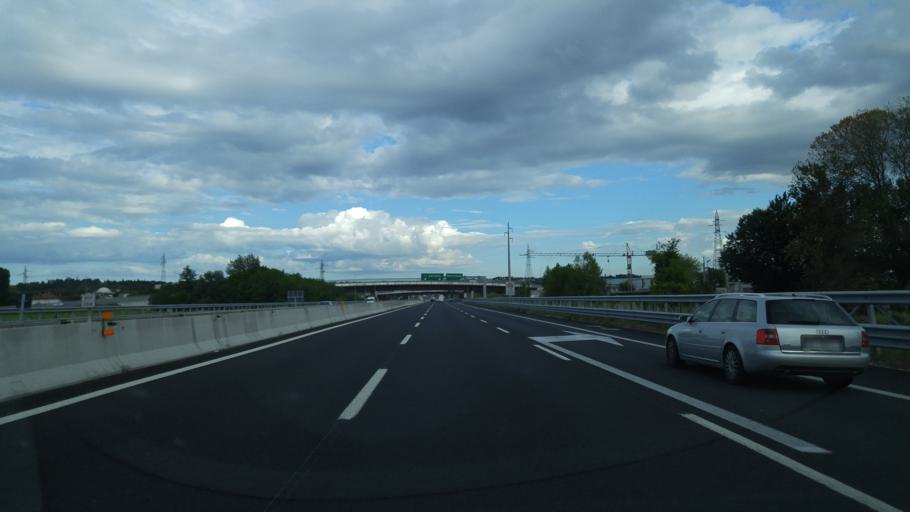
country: IT
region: Emilia-Romagna
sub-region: Provincia di Rimini
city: Riccione
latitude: 43.9889
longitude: 12.6316
